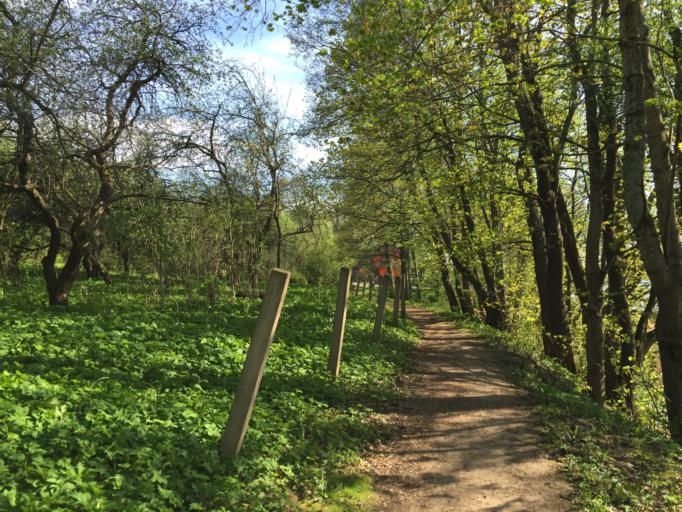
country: LV
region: Limbazu Rajons
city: Limbazi
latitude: 57.4938
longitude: 24.7058
